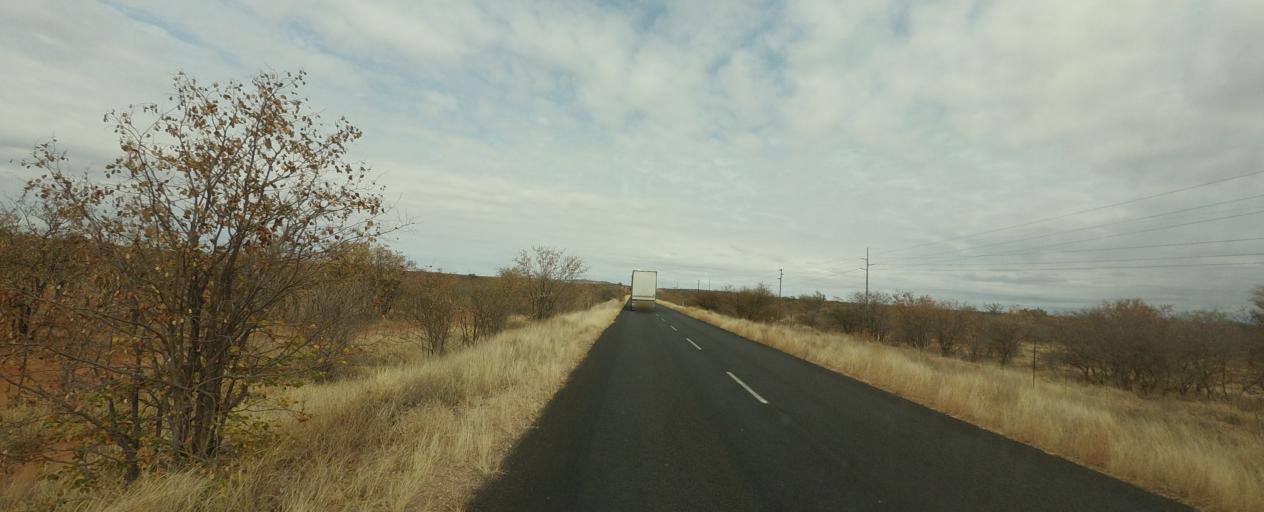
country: ZW
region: Matabeleland South
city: Beitbridge
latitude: -22.4301
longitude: 29.4360
